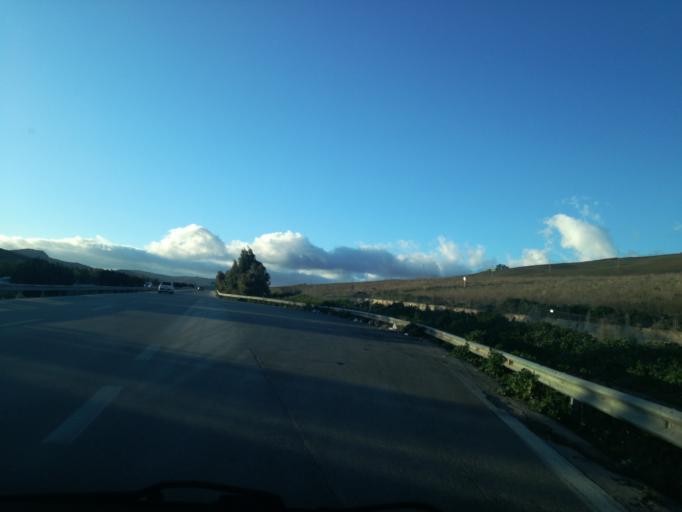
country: IT
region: Sicily
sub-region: Palermo
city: Castellana Sicula
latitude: 37.7402
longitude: 14.0023
